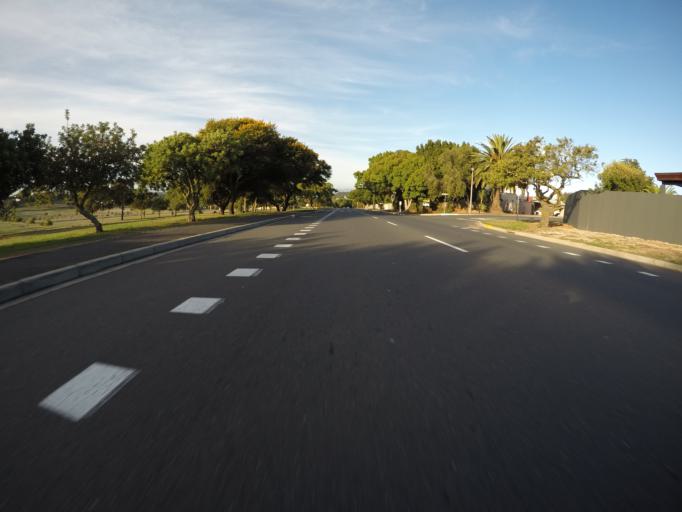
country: ZA
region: Western Cape
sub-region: City of Cape Town
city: Kraaifontein
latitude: -33.8661
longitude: 18.6544
